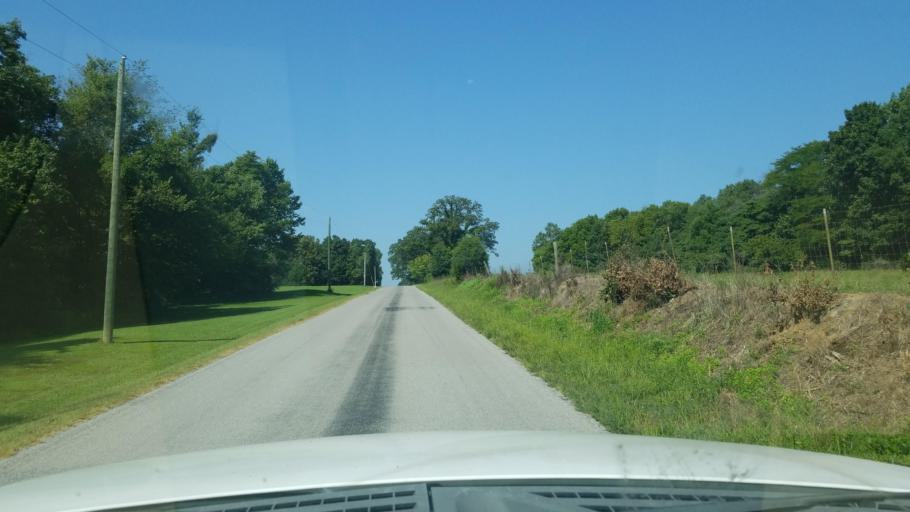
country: US
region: Illinois
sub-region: Saline County
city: Harrisburg
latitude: 37.8926
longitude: -88.6275
